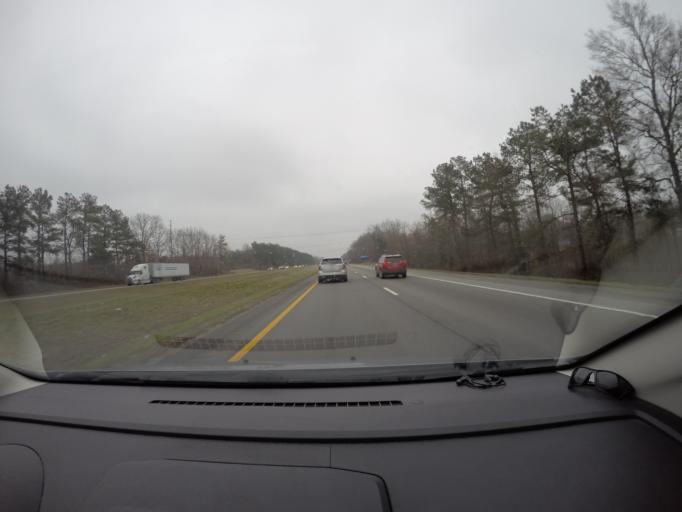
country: US
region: Tennessee
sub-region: Coffee County
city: New Union
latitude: 35.5130
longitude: -86.1138
